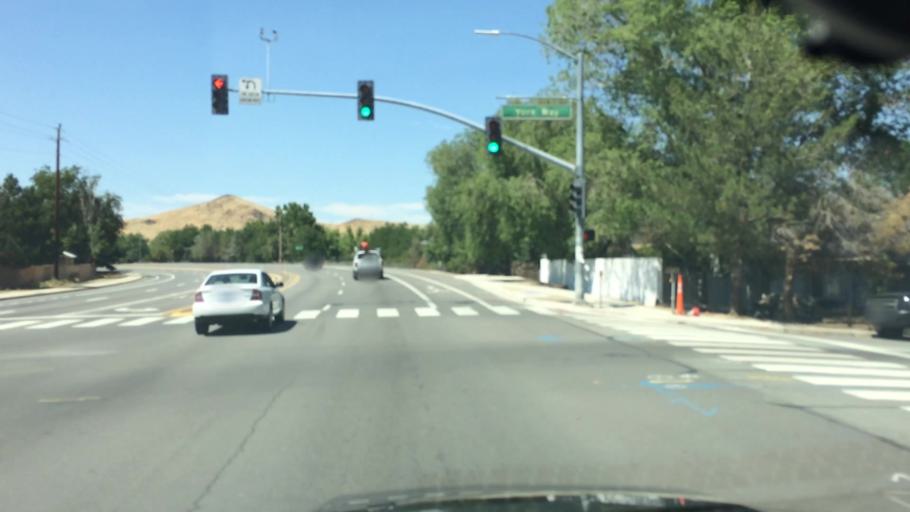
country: US
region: Nevada
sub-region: Washoe County
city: Sparks
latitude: 39.5527
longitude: -119.7337
